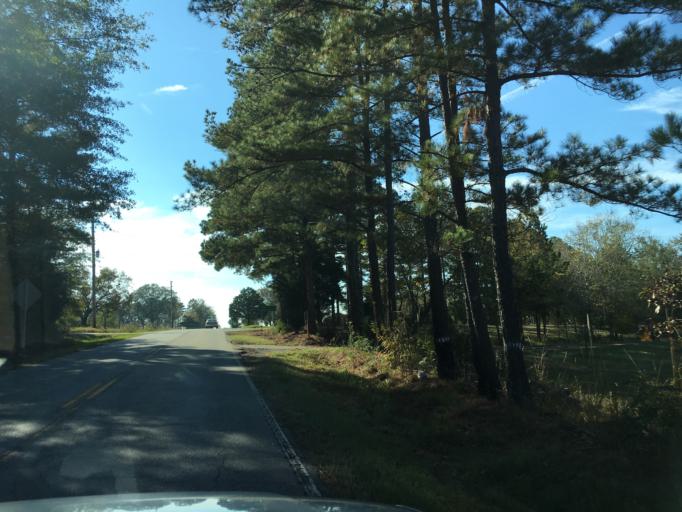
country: US
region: South Carolina
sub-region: Anderson County
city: Iva
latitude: 34.3391
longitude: -82.7594
